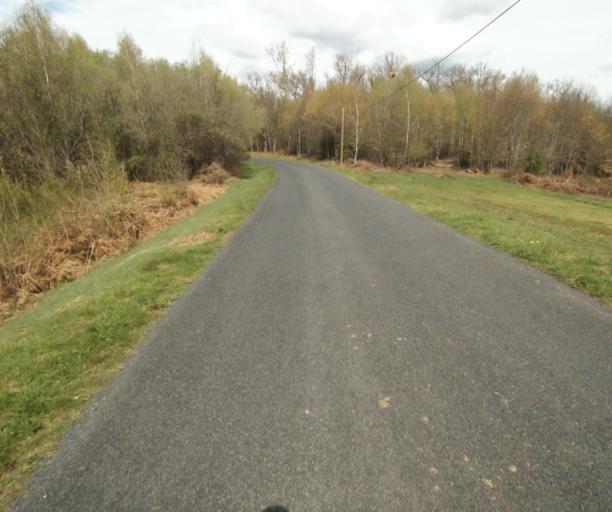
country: FR
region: Limousin
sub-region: Departement de la Correze
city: Argentat
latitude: 45.1953
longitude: 1.8897
